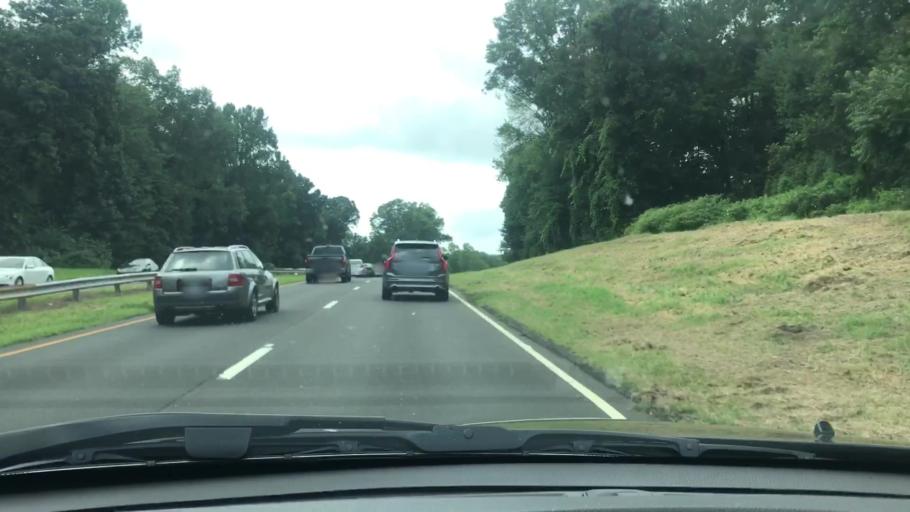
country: US
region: Connecticut
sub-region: Fairfield County
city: New Canaan
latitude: 41.1220
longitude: -73.4758
